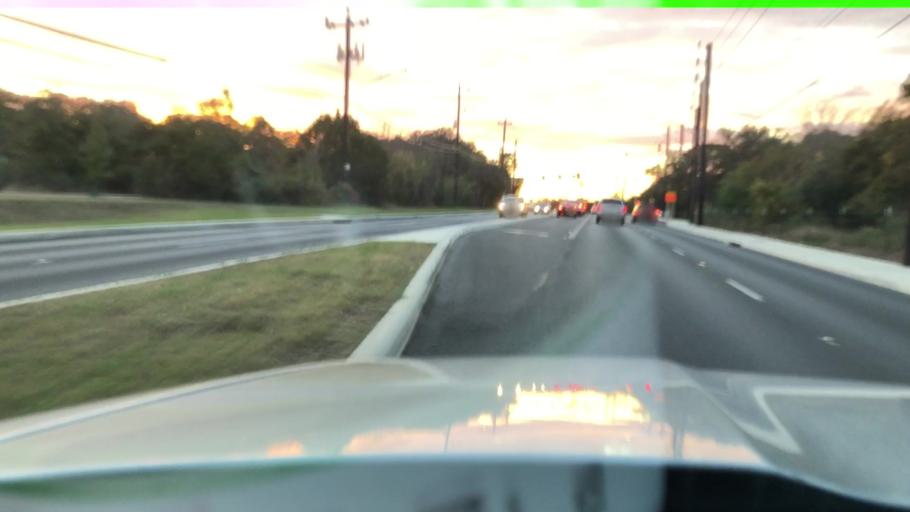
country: US
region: Texas
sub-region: Bexar County
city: Helotes
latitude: 29.5710
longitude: -98.6421
